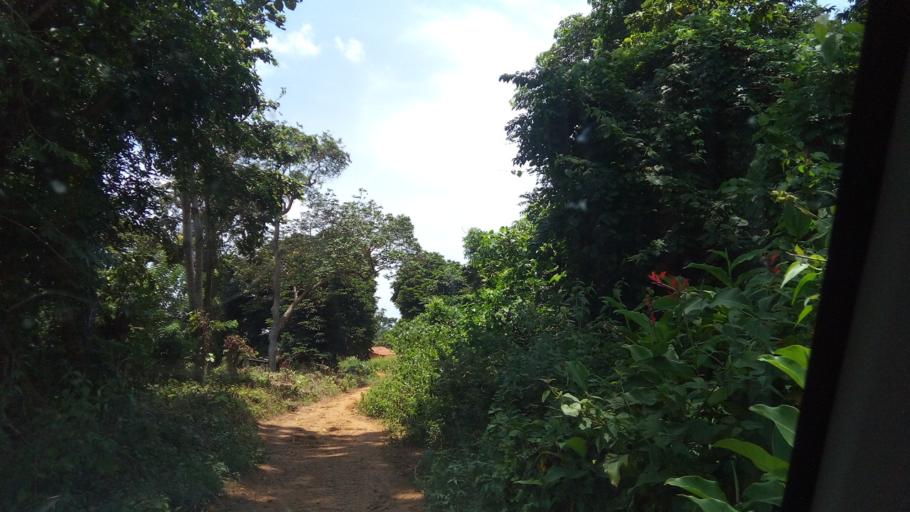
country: AO
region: Zaire
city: Mbanza Congo
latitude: -5.8040
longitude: 14.2448
